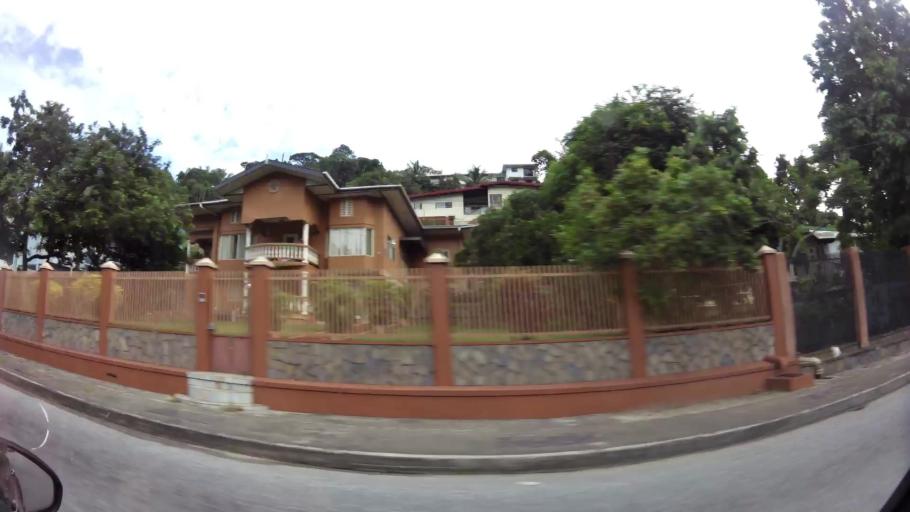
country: TT
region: San Juan/Laventille
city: Laventille
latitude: 10.6799
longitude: -61.4558
